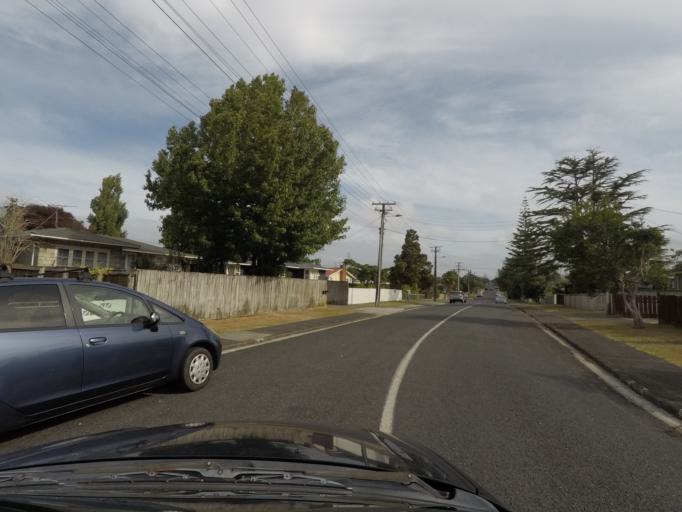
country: NZ
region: Auckland
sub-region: Auckland
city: Rosebank
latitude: -36.8910
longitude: 174.6682
